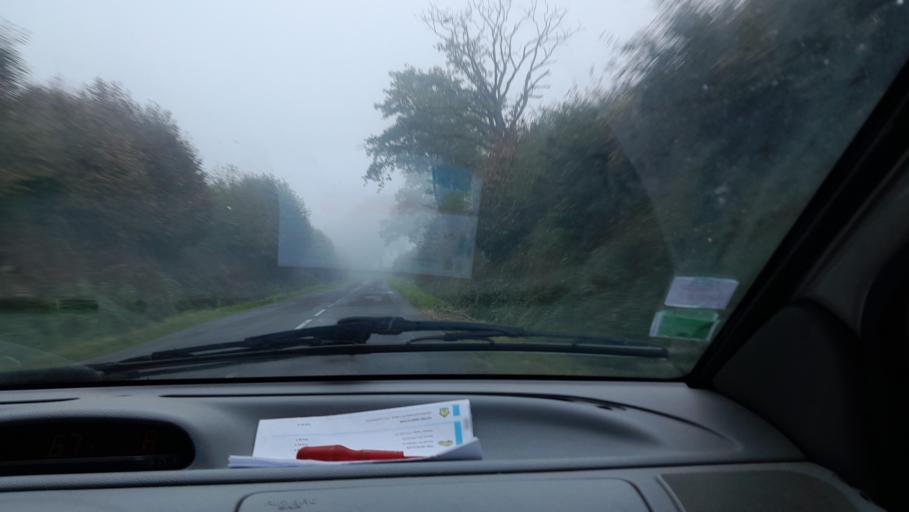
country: FR
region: Brittany
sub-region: Departement d'Ille-et-Vilaine
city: Le Pertre
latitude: 48.0402
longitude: -1.0357
